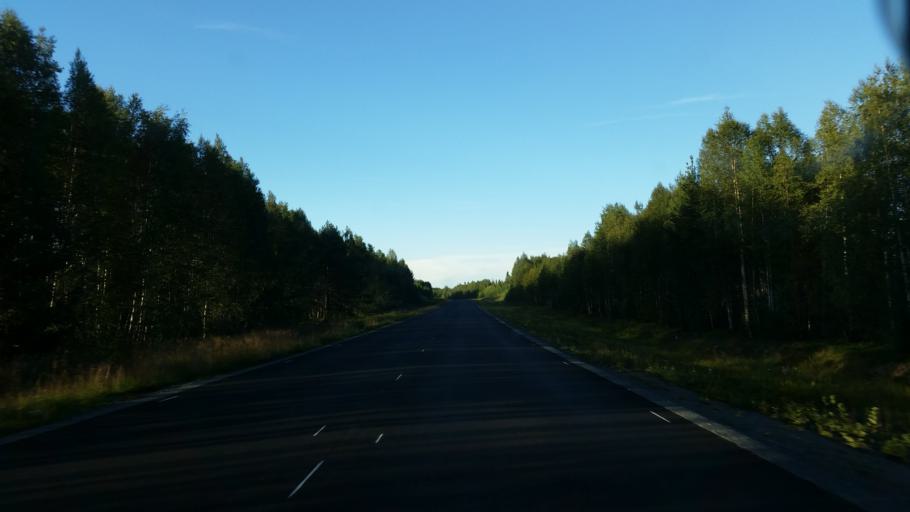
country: SE
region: Vaesterbotten
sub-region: Dorotea Kommun
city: Dorotea
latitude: 64.3249
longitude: 16.6226
